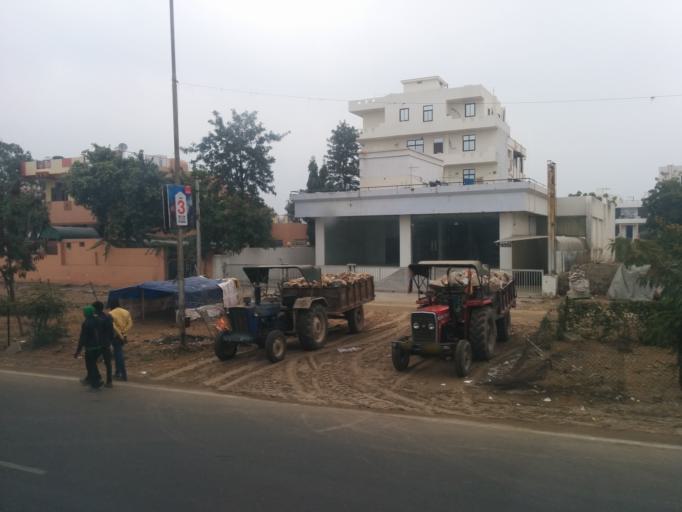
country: IN
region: Rajasthan
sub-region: Jaipur
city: Jaipur
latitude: 26.8780
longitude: 75.7717
